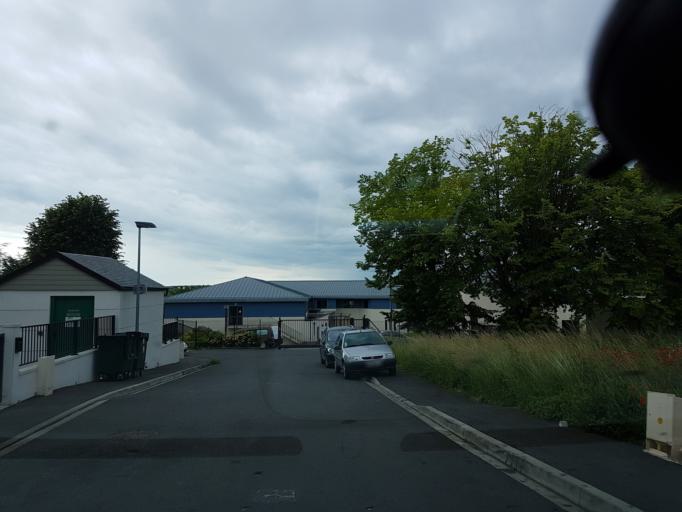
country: FR
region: Centre
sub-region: Departement du Cher
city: Bourges
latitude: 47.0953
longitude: 2.4085
